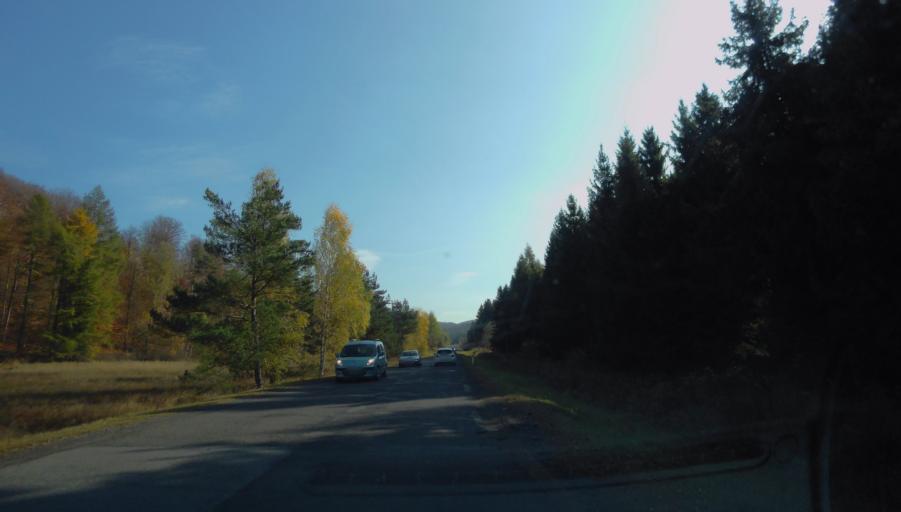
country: PL
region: Subcarpathian Voivodeship
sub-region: Powiat leski
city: Cisna
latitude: 49.2216
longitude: 22.2015
